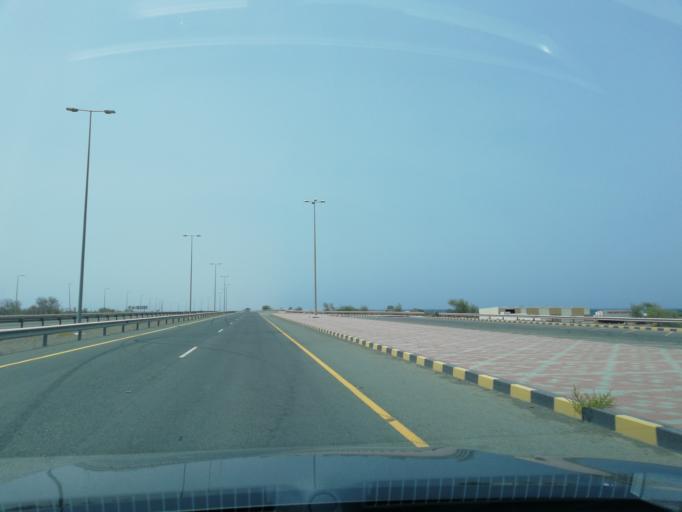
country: OM
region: Al Batinah
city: Shinas
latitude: 24.6550
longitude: 56.5133
